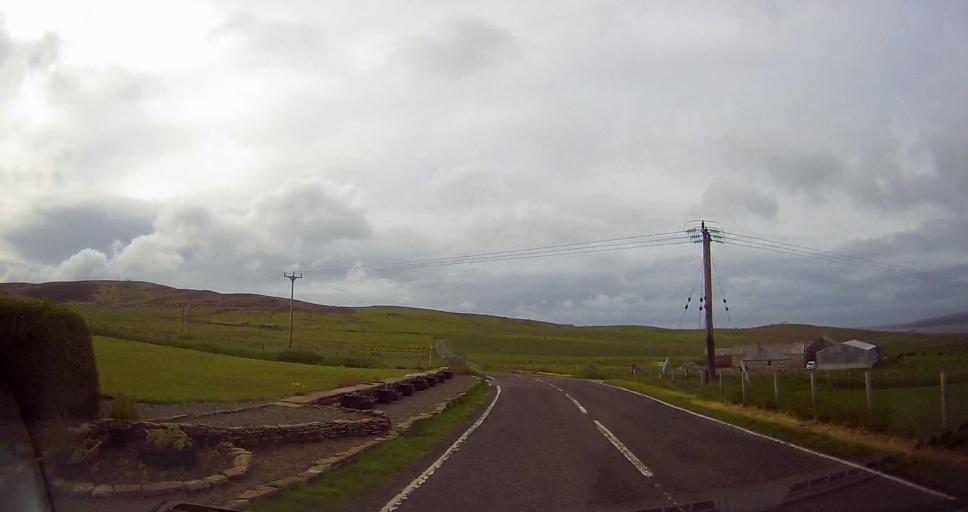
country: GB
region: Scotland
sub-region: Orkney Islands
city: Stromness
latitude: 58.9310
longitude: -3.2070
